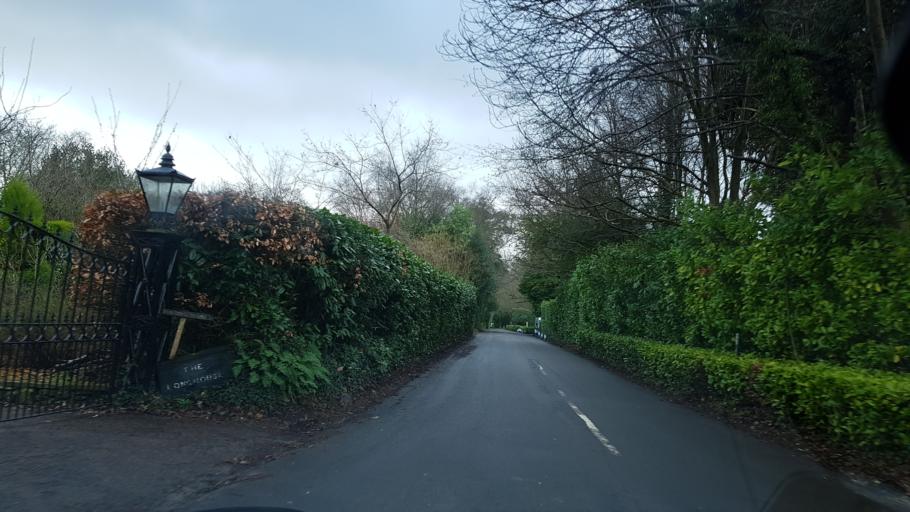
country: GB
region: England
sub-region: Surrey
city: Hindhead
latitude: 51.1026
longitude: -0.7422
